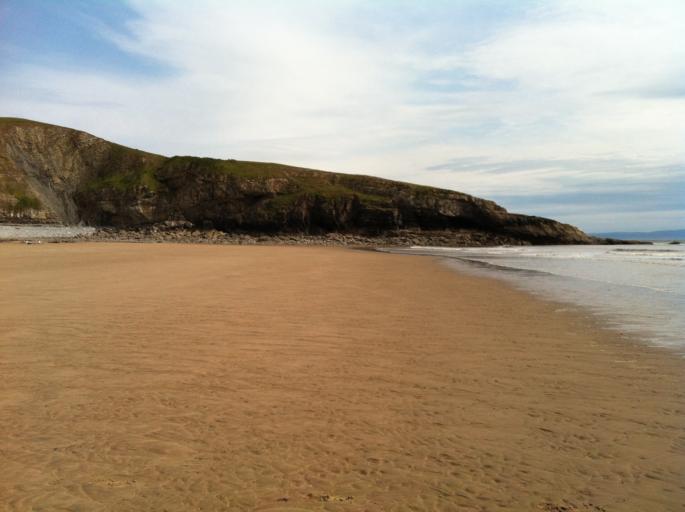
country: GB
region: Wales
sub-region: Bridgend county borough
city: Merthyr Mawr
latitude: 51.4442
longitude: -3.6079
